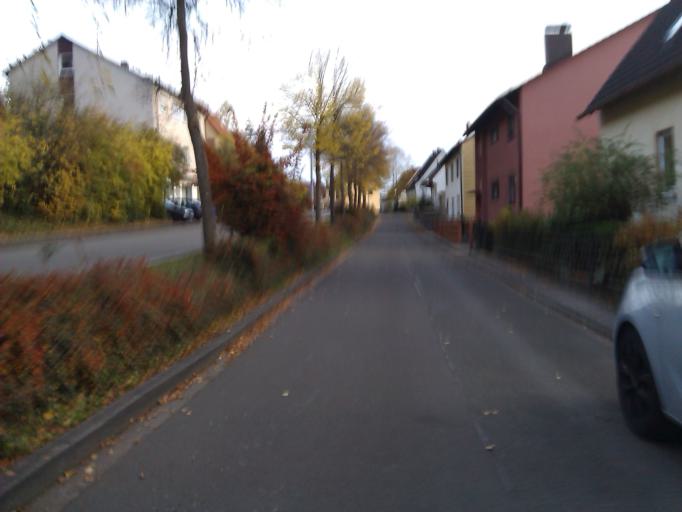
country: DE
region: Rheinland-Pfalz
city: Otterberg
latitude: 49.5052
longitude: 7.7655
